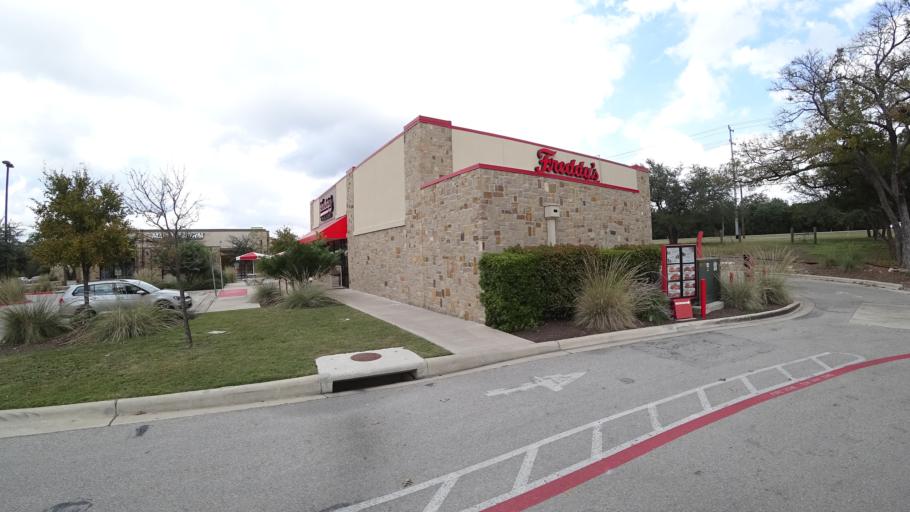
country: US
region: Texas
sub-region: Williamson County
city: Anderson Mill
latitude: 30.4230
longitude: -97.8455
